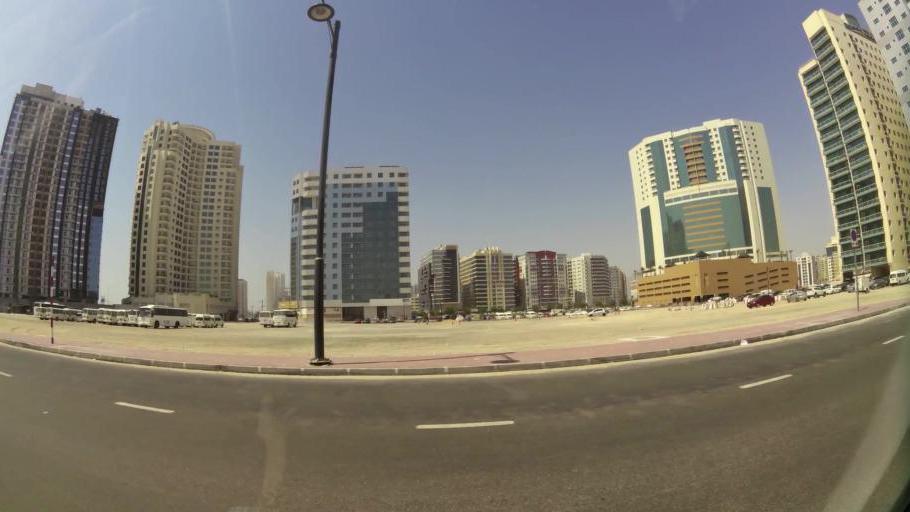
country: AE
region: Ash Shariqah
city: Sharjah
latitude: 25.2865
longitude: 55.3631
